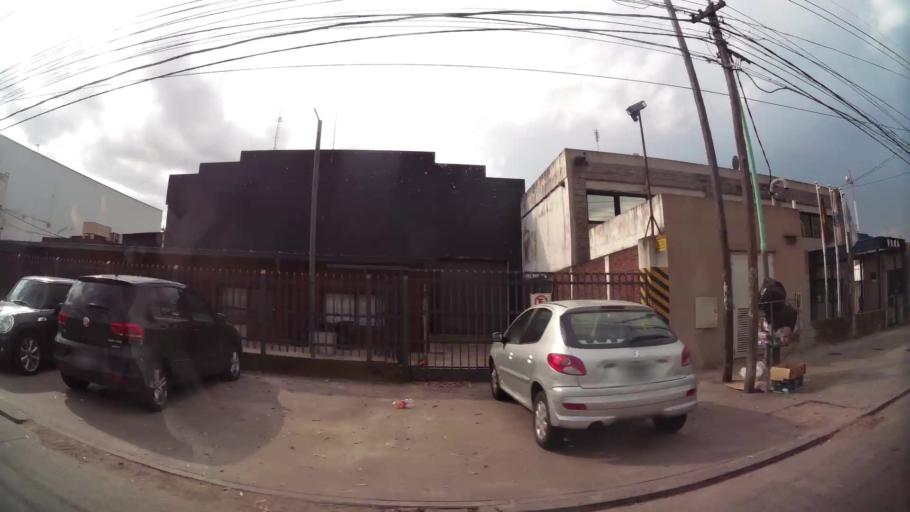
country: AR
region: Buenos Aires
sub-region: Partido de Tigre
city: Tigre
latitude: -34.4811
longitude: -58.6340
